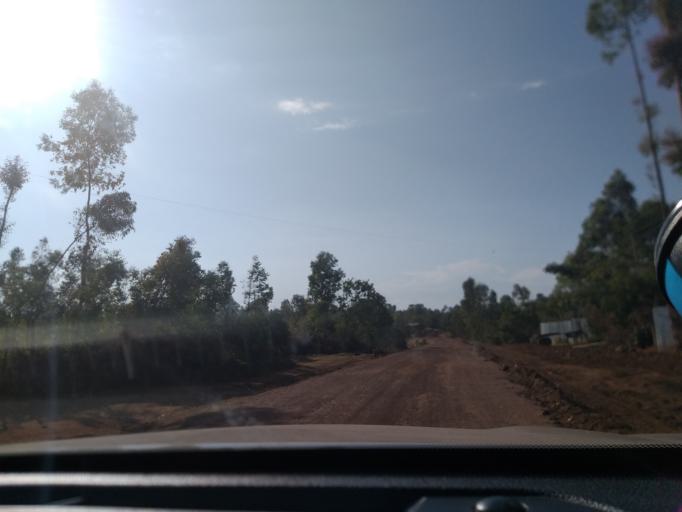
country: ET
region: Oromiya
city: Shashemene
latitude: 7.4289
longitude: 38.8065
